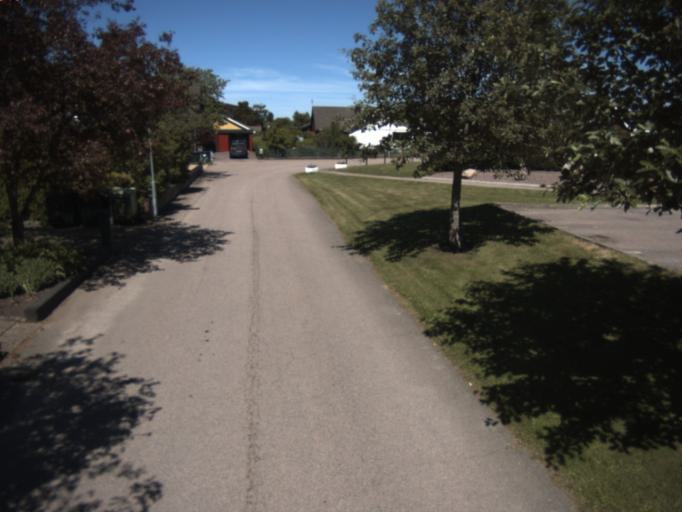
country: SE
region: Skane
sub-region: Helsingborg
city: Morarp
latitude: 56.0531
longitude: 12.8762
